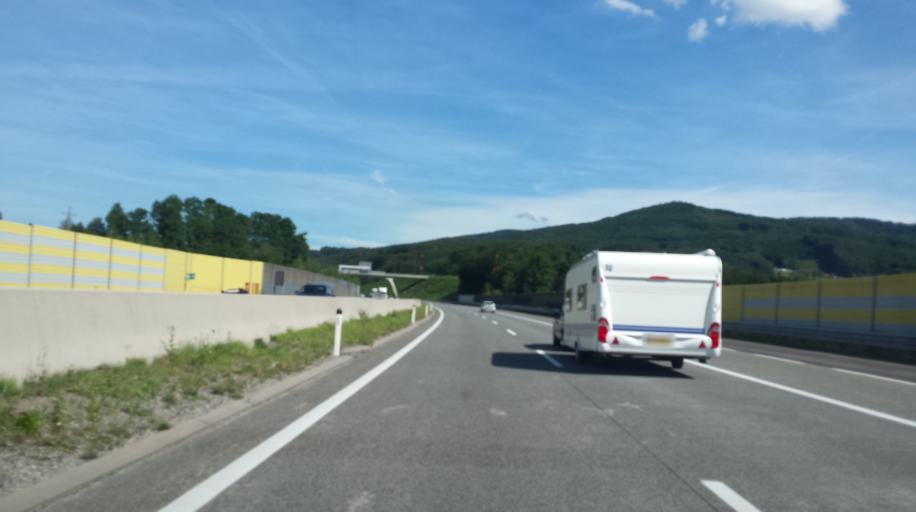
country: AT
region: Upper Austria
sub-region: Politischer Bezirk Vocklabruck
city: Aurach am Hongar
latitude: 47.9497
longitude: 13.6694
